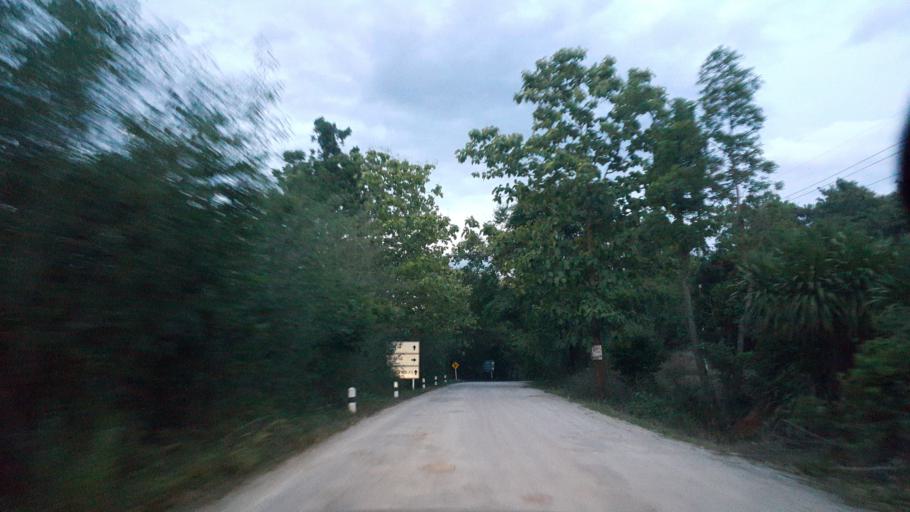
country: TH
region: Loei
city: Phu Ruea
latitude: 17.5334
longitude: 101.2262
